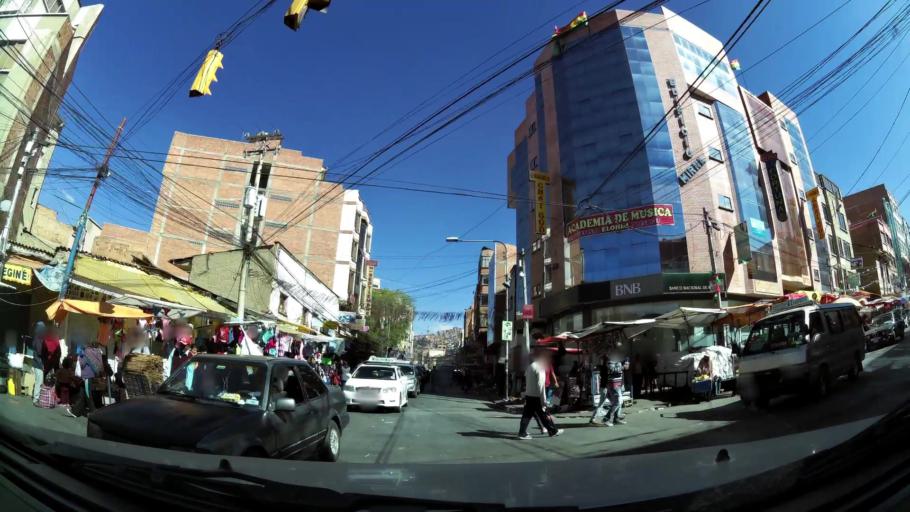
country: BO
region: La Paz
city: La Paz
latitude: -16.4953
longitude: -68.1441
